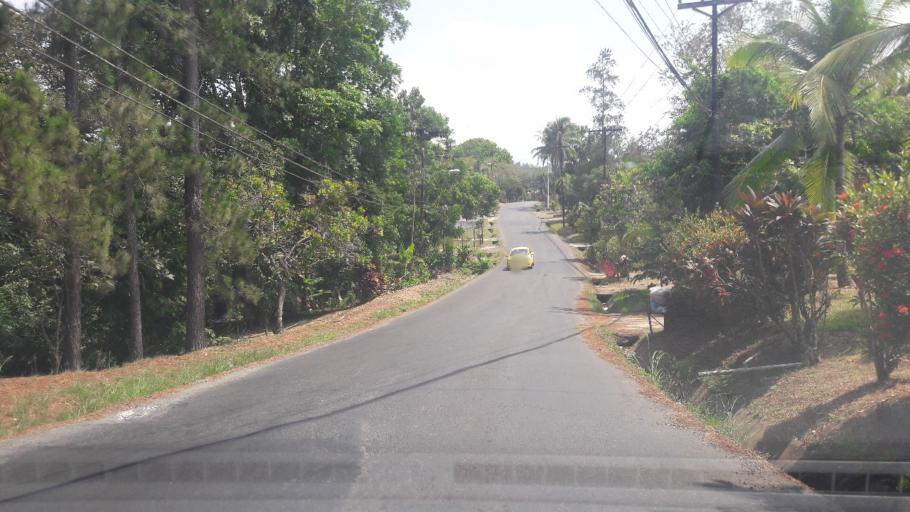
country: PA
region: Panama
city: Alcalde Diaz
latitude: 9.1354
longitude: -79.5513
